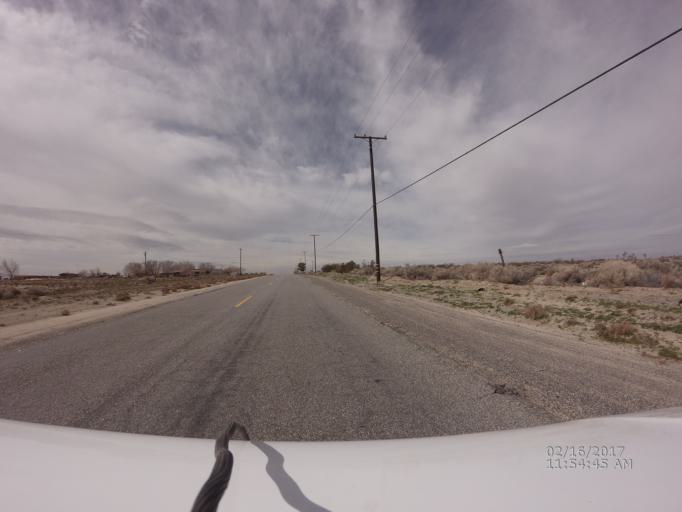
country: US
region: California
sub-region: Los Angeles County
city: Lake Los Angeles
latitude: 34.6900
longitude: -117.8926
